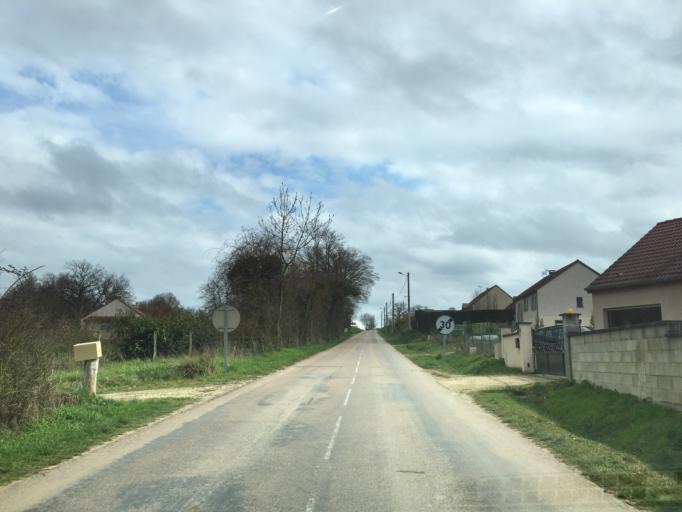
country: FR
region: Bourgogne
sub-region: Departement de l'Yonne
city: Pourrain
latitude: 47.7944
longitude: 3.3849
